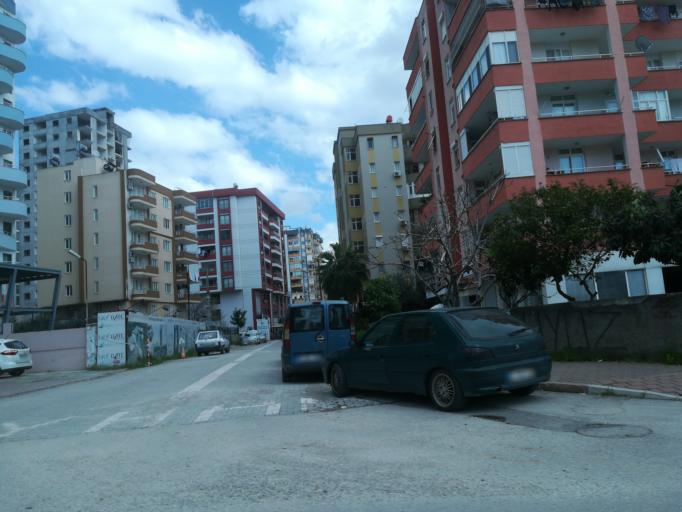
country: TR
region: Adana
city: Adana
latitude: 37.0367
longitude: 35.3127
